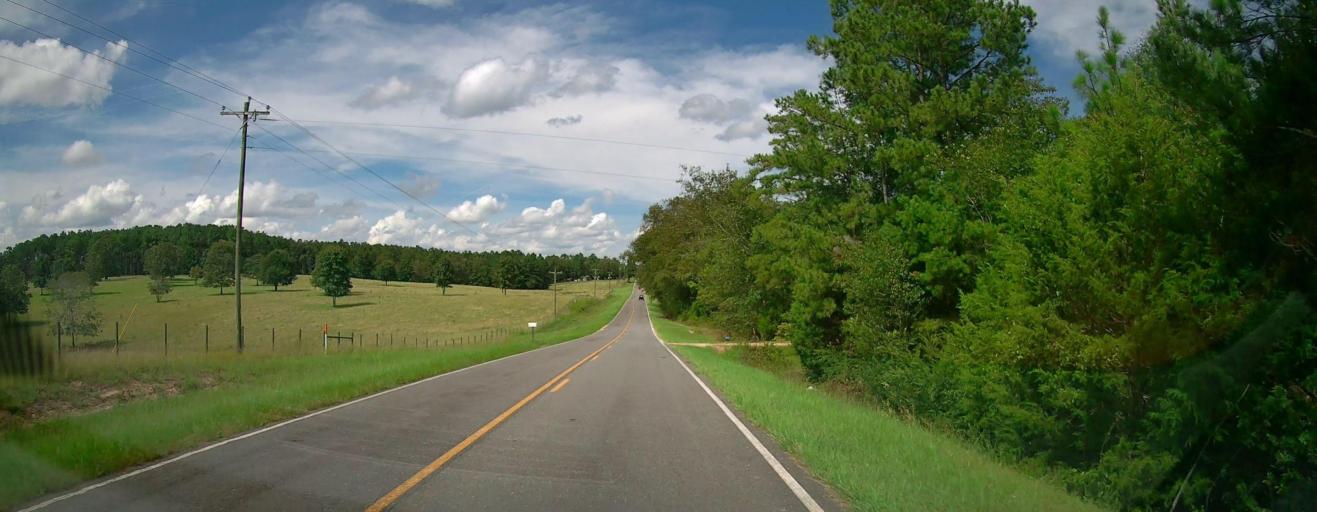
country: US
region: Georgia
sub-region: Taylor County
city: Butler
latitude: 32.4499
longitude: -84.1958
